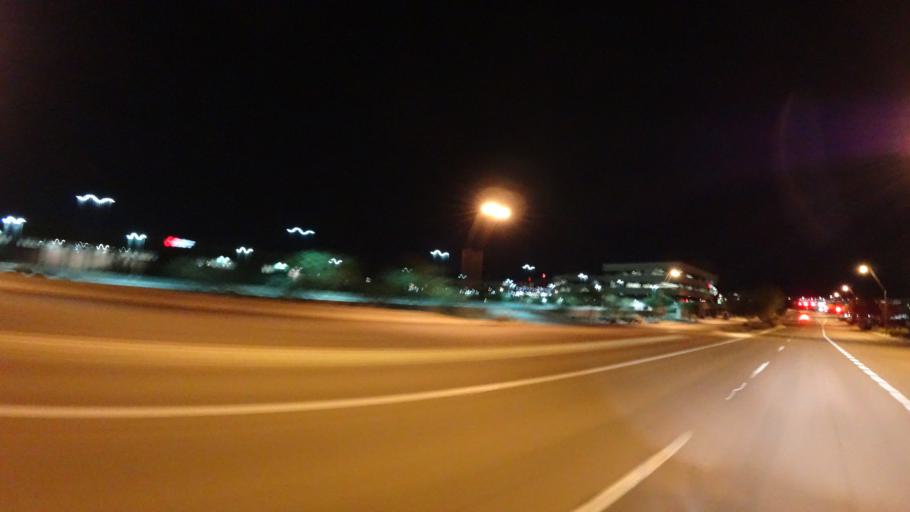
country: US
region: Arizona
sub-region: Maricopa County
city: Tempe Junction
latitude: 33.4413
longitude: -111.9587
